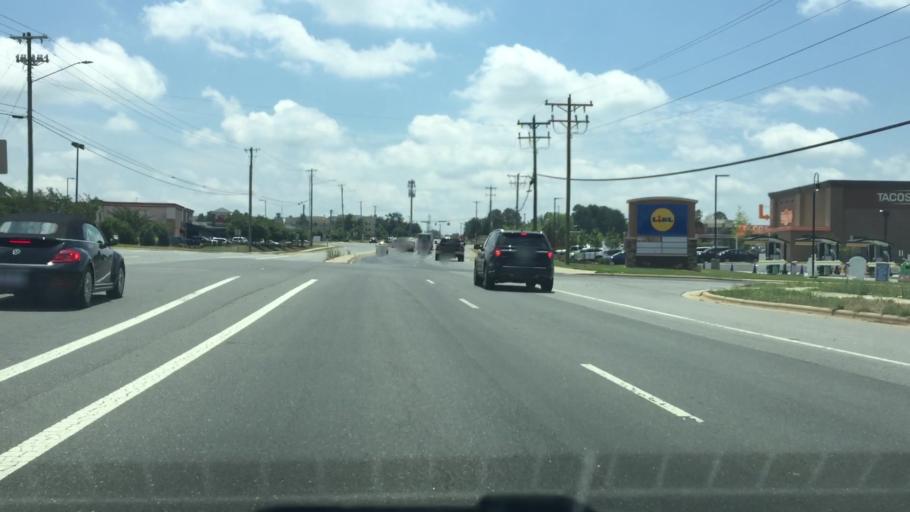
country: US
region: North Carolina
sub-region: Cabarrus County
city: Harrisburg
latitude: 35.3769
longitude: -80.7298
